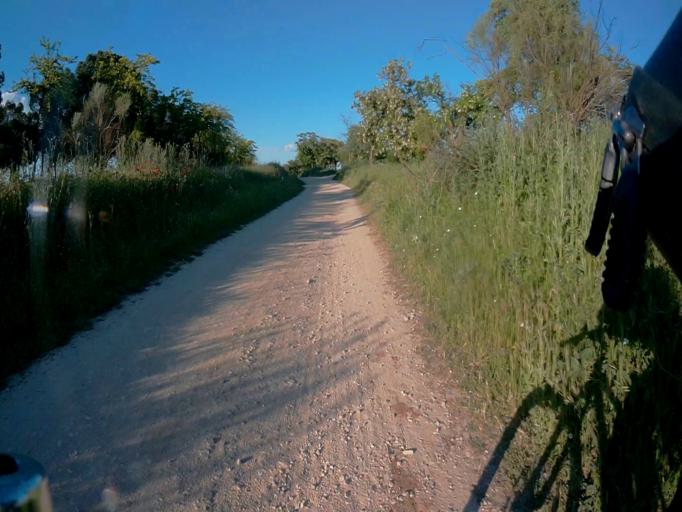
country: ES
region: Madrid
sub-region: Provincia de Madrid
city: Fuenlabrada
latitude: 40.3142
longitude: -3.8004
